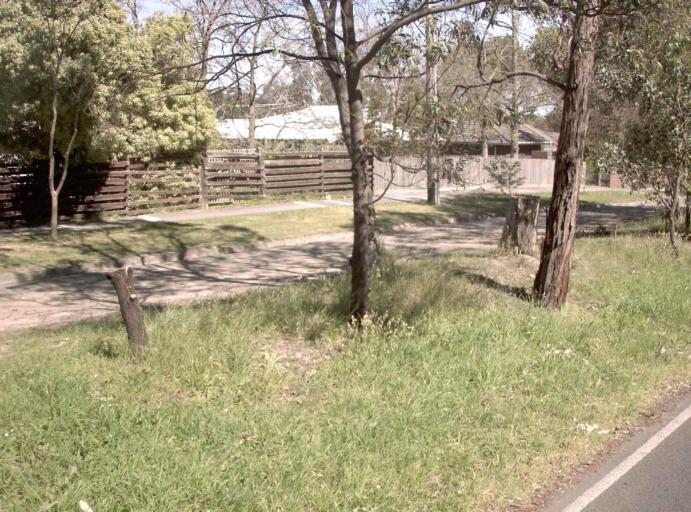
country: AU
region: Victoria
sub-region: Maroondah
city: Croydon South
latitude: -37.8091
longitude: 145.2702
